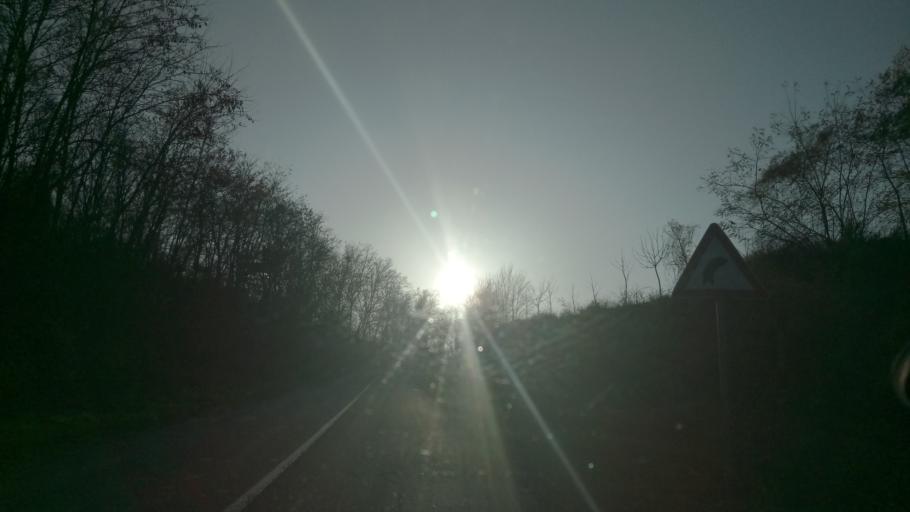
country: RS
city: Beska
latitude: 45.1172
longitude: 20.0539
